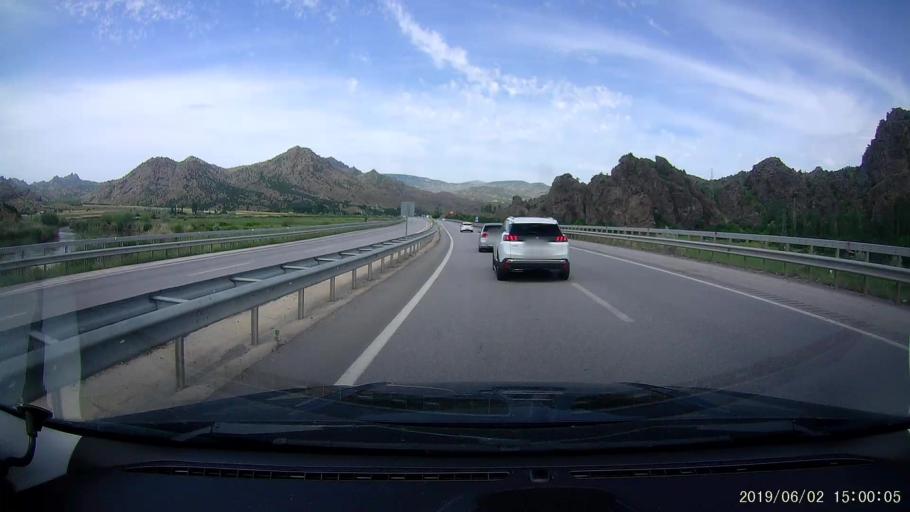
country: TR
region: Corum
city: Osmancik
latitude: 40.9739
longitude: 34.7070
